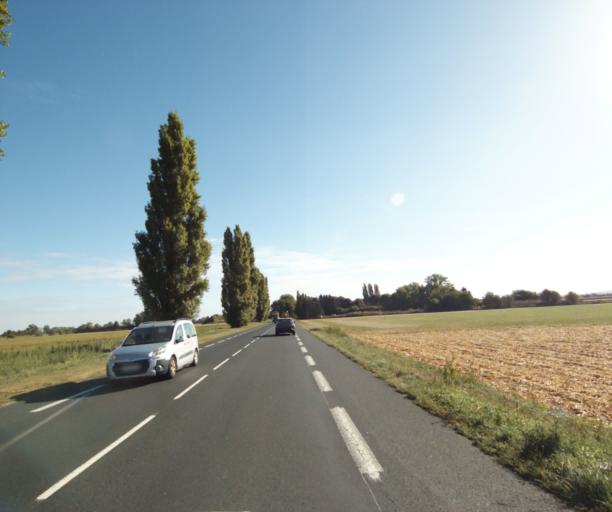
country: FR
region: Auvergne
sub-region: Departement du Puy-de-Dome
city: Aulnat
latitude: 45.8141
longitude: 3.1669
